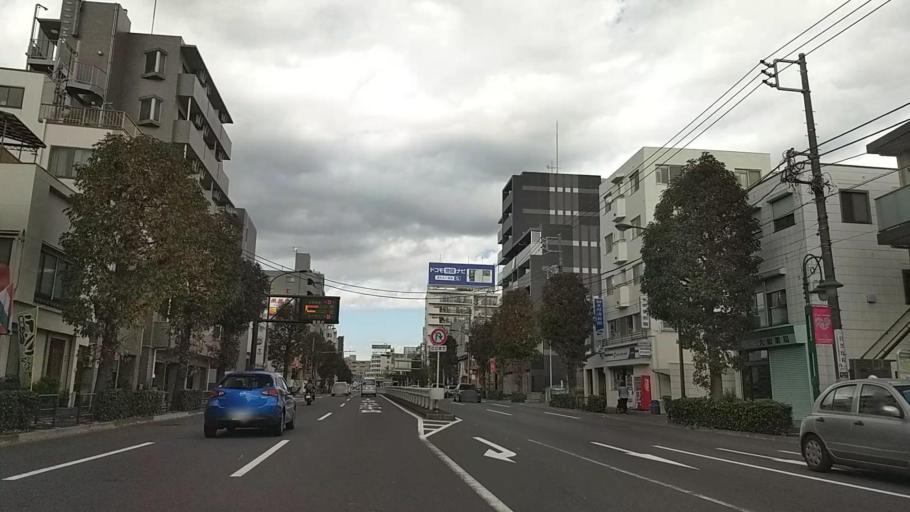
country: JP
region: Tokyo
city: Tokyo
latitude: 35.6153
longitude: 139.6366
